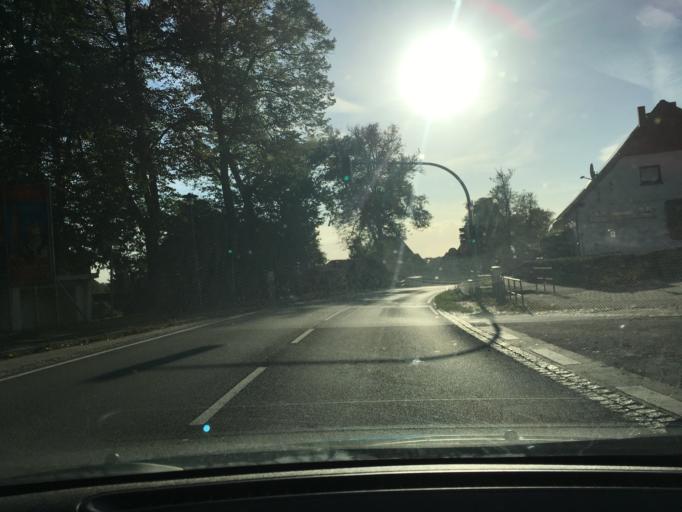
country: DE
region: Lower Saxony
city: Neu Darchau
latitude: 53.3813
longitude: 10.8916
